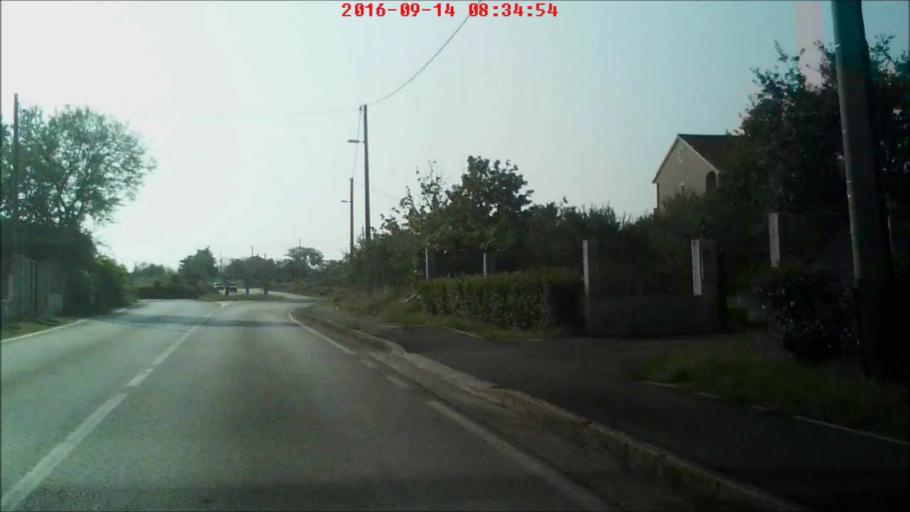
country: HR
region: Zadarska
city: Policnik
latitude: 44.1494
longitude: 15.3255
